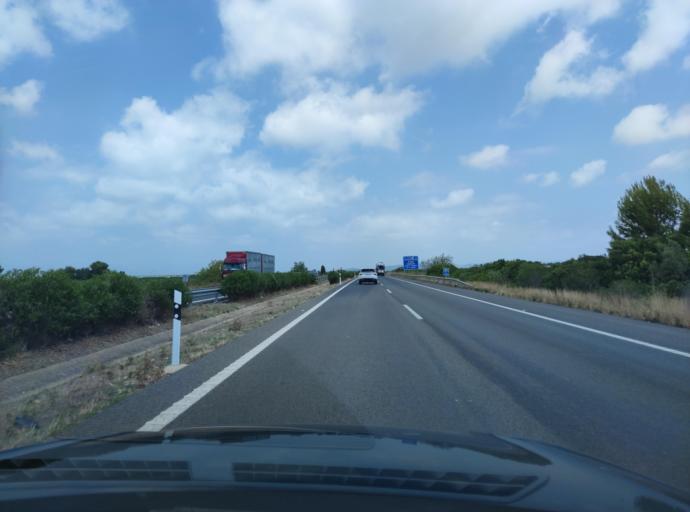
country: ES
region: Valencia
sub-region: Provincia de Castello
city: Vinaros
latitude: 40.5108
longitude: 0.4153
